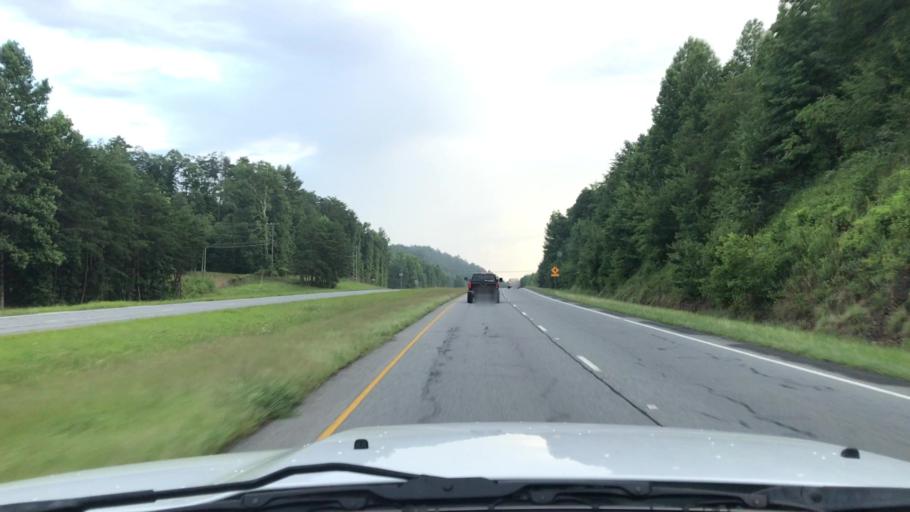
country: US
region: Georgia
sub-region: Fannin County
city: Blue Ridge
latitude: 34.8191
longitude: -84.3629
